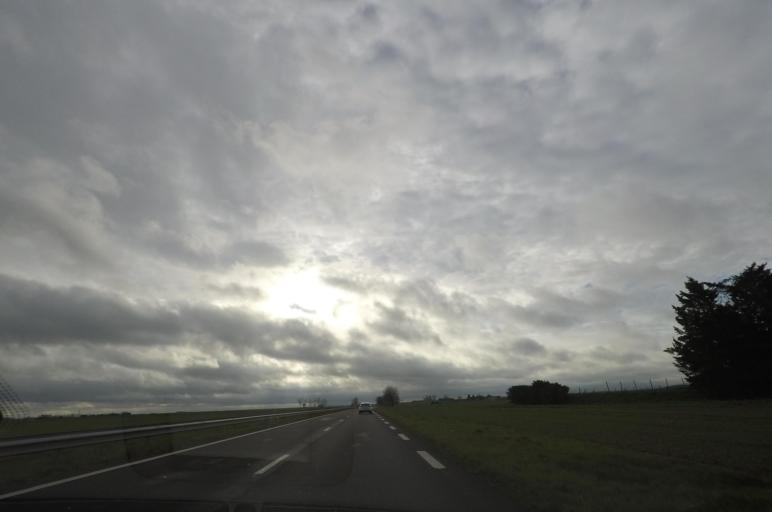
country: FR
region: Centre
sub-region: Departement du Loir-et-Cher
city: Vendome
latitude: 47.7245
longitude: 1.1521
